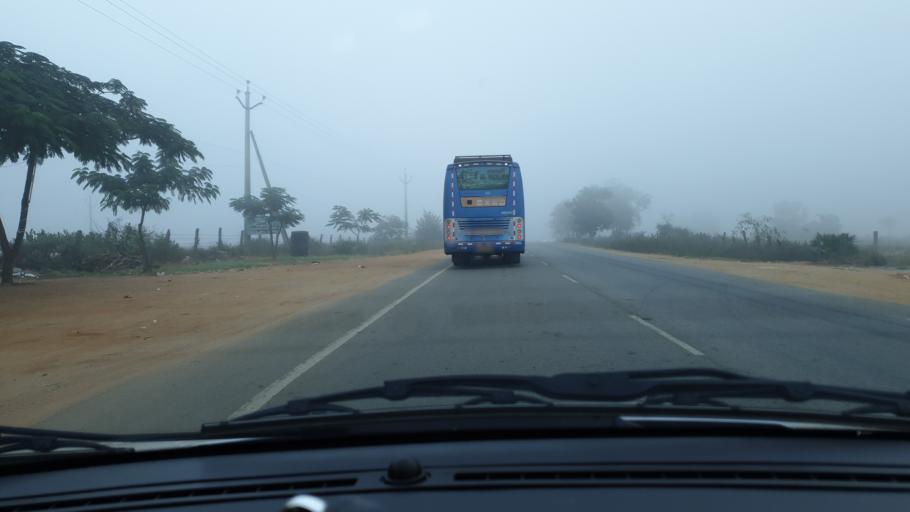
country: IN
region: Telangana
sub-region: Mahbubnagar
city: Nagar Karnul
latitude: 16.6639
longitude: 78.5432
